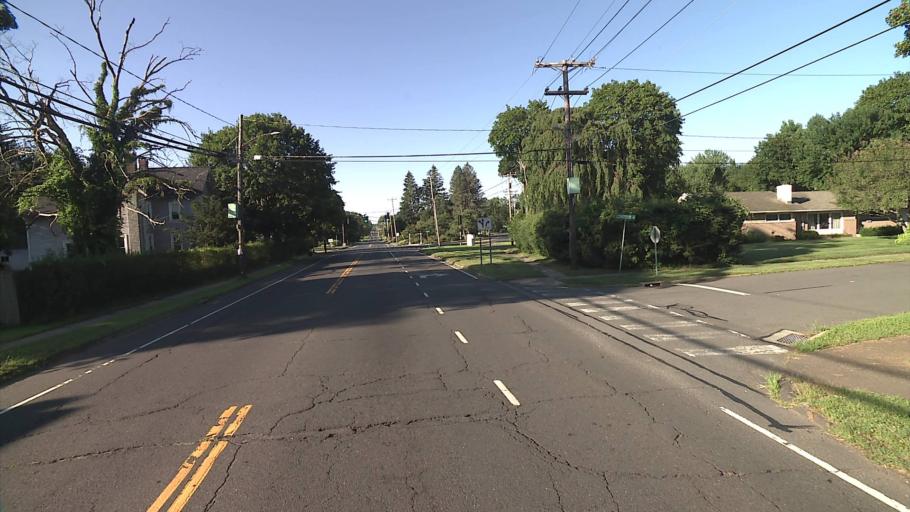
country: US
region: Connecticut
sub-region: New Haven County
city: Cheshire Village
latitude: 41.5161
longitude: -72.8982
